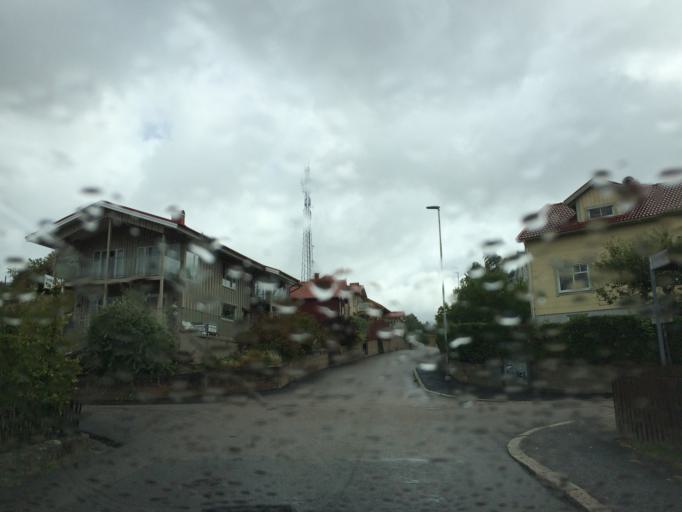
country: SE
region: Vaestra Goetaland
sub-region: Trollhattan
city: Trollhattan
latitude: 58.2872
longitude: 12.2760
